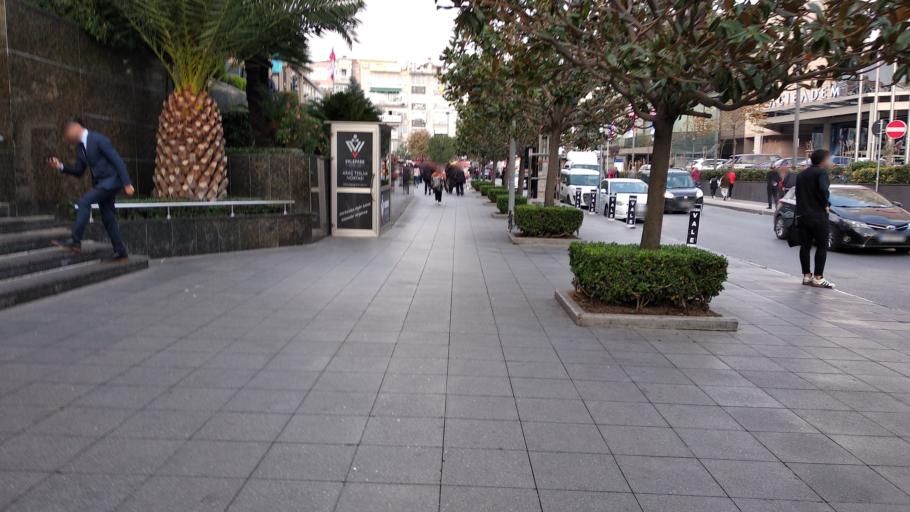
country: TR
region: Istanbul
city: Bahcelievler
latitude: 40.9771
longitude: 28.8723
